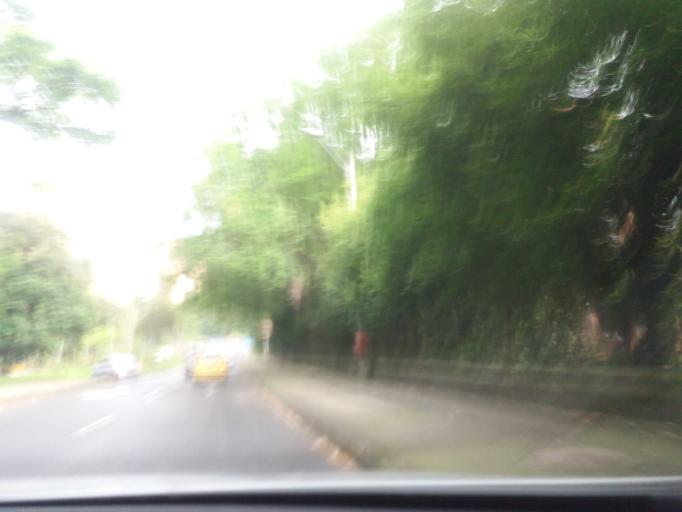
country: CO
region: Antioquia
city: Envigado
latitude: 6.2048
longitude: -75.5650
